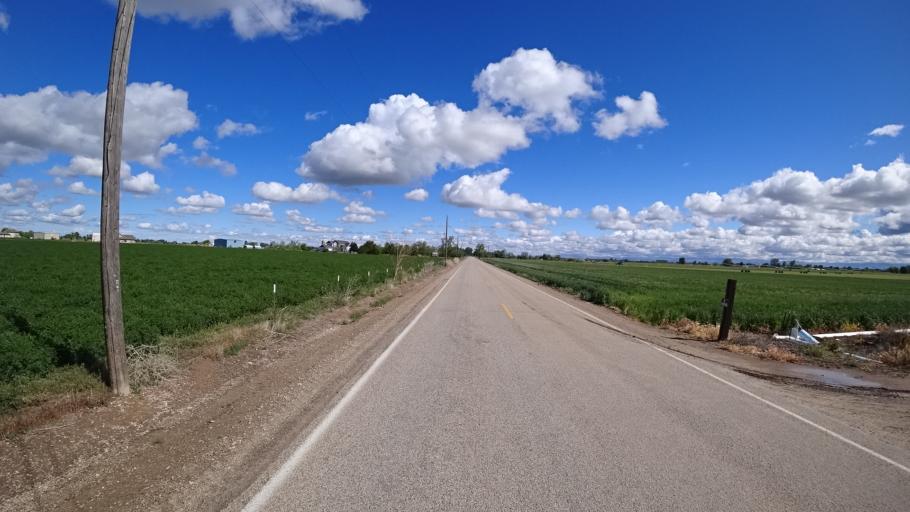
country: US
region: Idaho
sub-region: Ada County
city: Kuna
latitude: 43.4817
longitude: -116.4536
